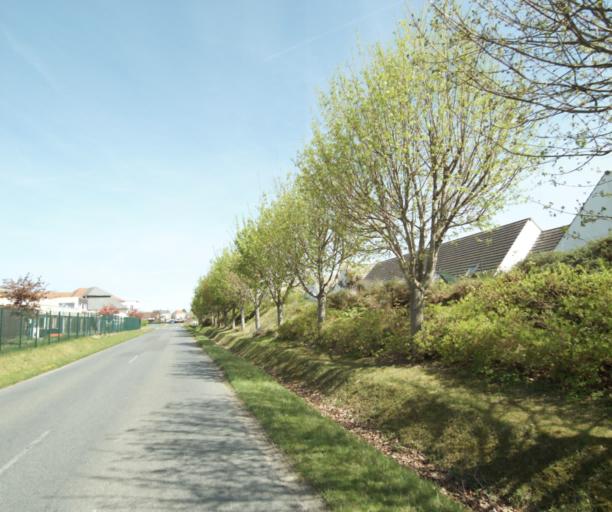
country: FR
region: Ile-de-France
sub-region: Departement de Seine-et-Marne
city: Nangis
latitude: 48.5537
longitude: 3.0039
